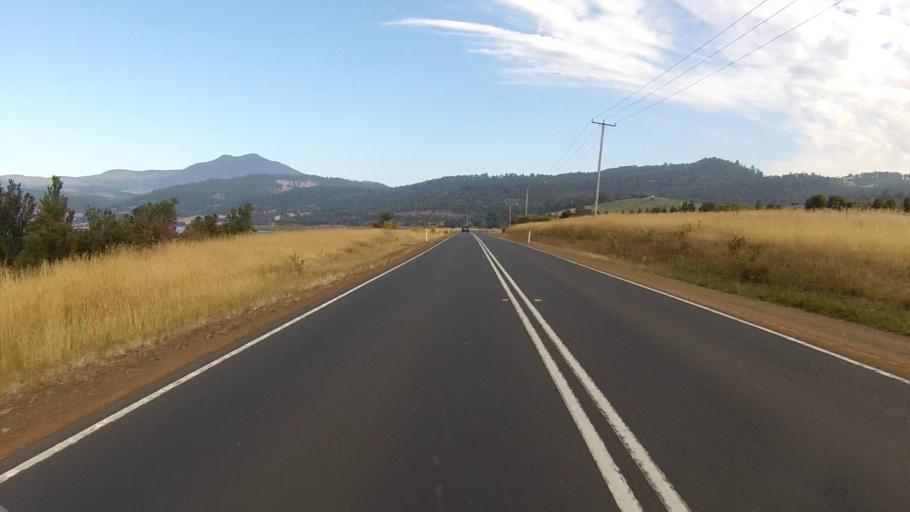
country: AU
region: Tasmania
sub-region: Brighton
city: Bridgewater
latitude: -42.7307
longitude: 147.2093
